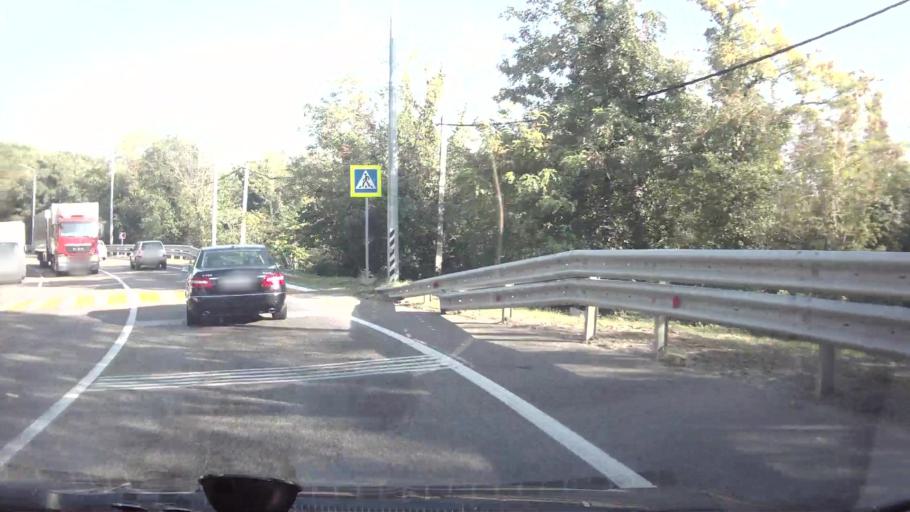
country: RU
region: Krasnodarskiy
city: Shepsi
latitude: 44.0227
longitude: 39.1578
